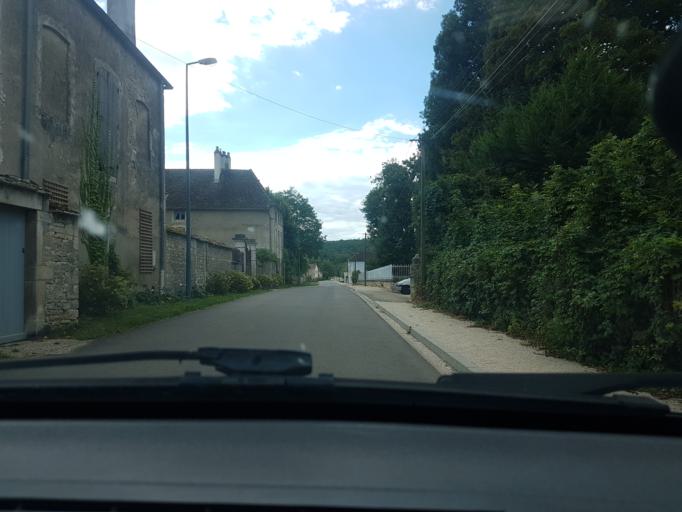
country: FR
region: Bourgogne
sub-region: Departement de Saone-et-Loire
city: Fontaines
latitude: 46.8477
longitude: 4.7675
